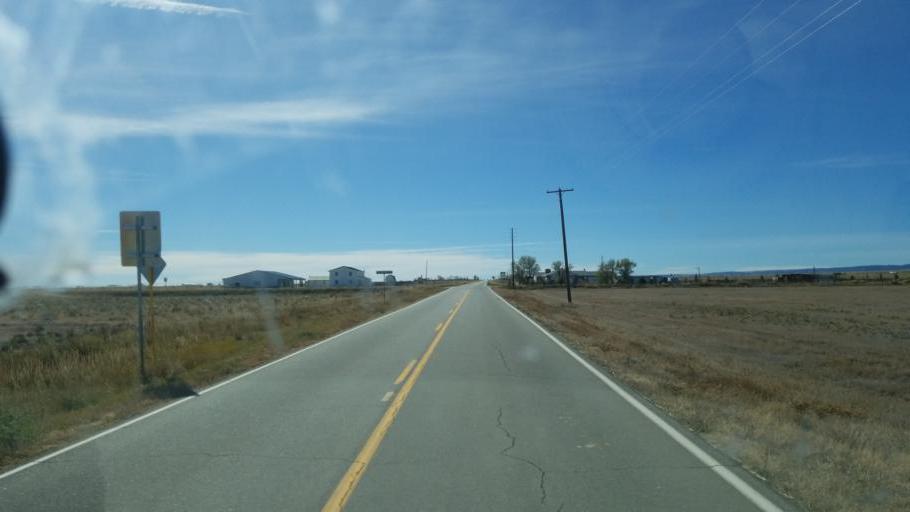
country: US
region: Colorado
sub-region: Rio Grande County
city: Monte Vista
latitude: 37.4310
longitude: -106.1481
